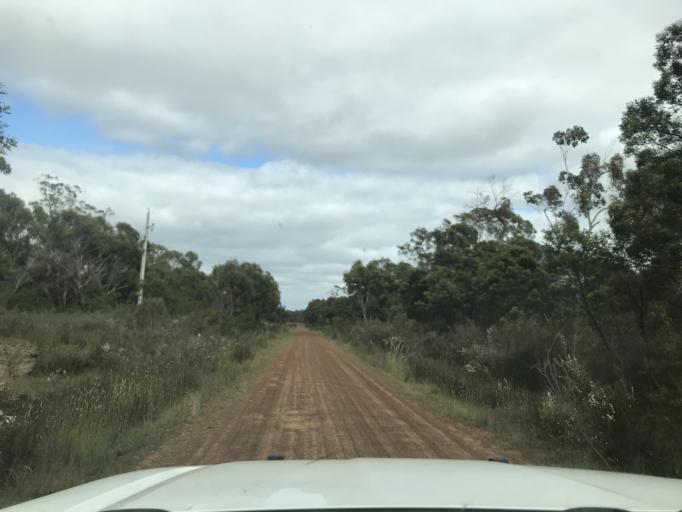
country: AU
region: South Australia
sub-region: Wattle Range
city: Penola
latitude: -37.3344
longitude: 141.4192
